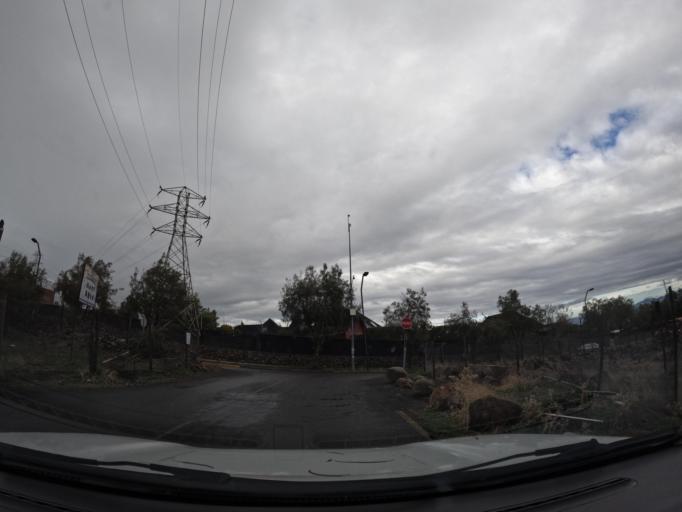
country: CL
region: Santiago Metropolitan
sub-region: Provincia de Santiago
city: Villa Presidente Frei, Nunoa, Santiago, Chile
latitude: -33.4982
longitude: -70.5194
